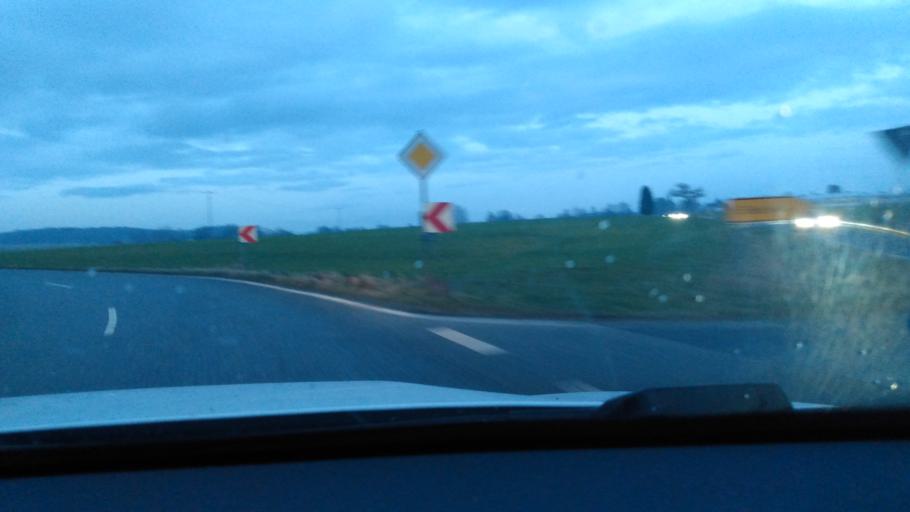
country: DE
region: Rheinland-Pfalz
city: Kircheib
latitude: 50.6924
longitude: 7.4417
